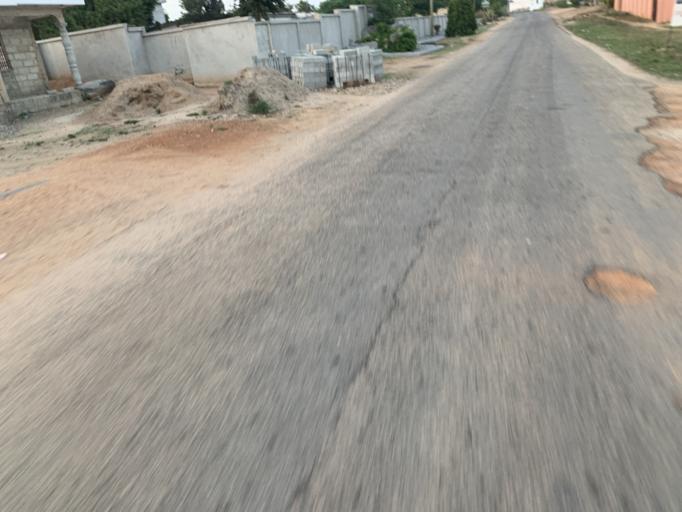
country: GH
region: Central
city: Winneba
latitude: 5.3599
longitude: -0.6229
